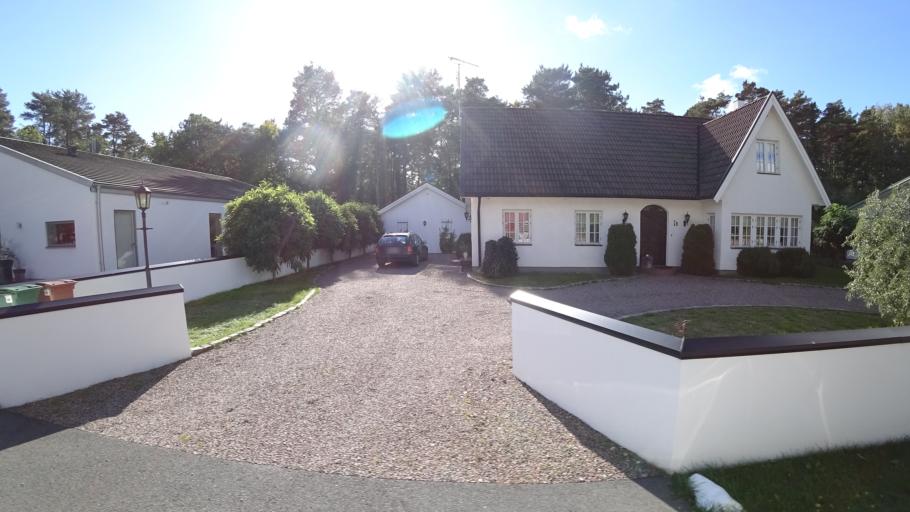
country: SE
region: Skane
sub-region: Kavlinge Kommun
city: Loddekopinge
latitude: 55.7549
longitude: 12.9900
